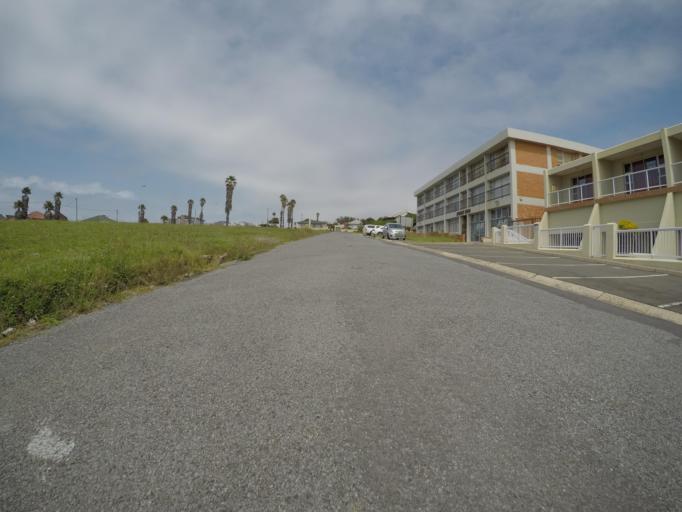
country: ZA
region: Eastern Cape
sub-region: Buffalo City Metropolitan Municipality
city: East London
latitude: -32.9395
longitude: 28.0305
